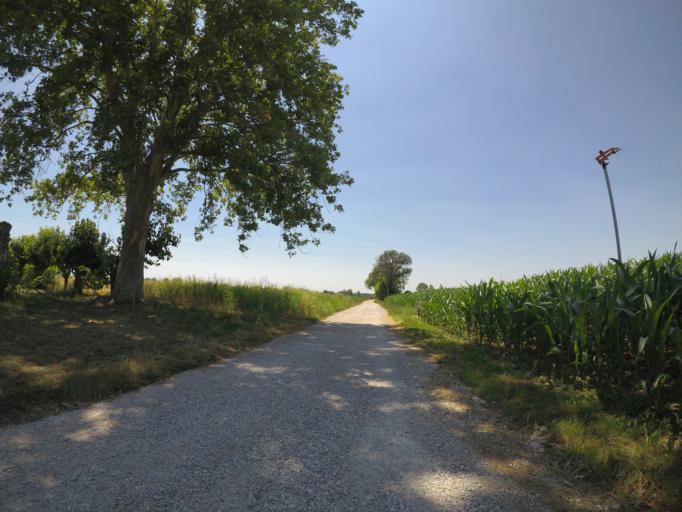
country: IT
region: Friuli Venezia Giulia
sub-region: Provincia di Udine
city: Talmassons
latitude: 45.9286
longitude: 13.0973
